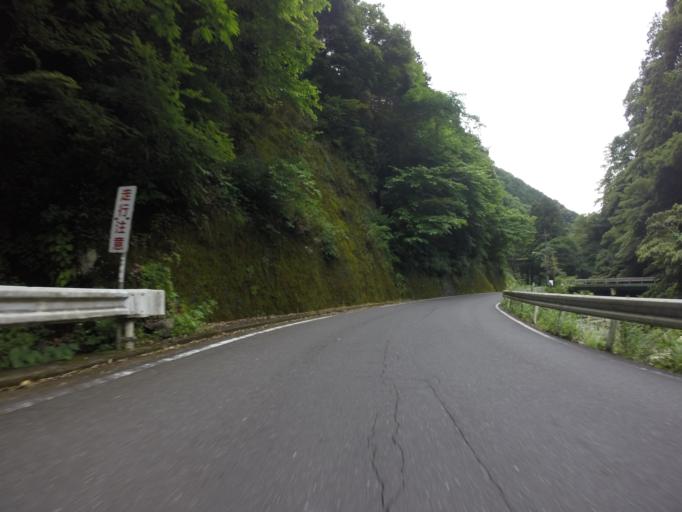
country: JP
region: Shizuoka
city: Shizuoka-shi
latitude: 35.0264
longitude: 138.2886
